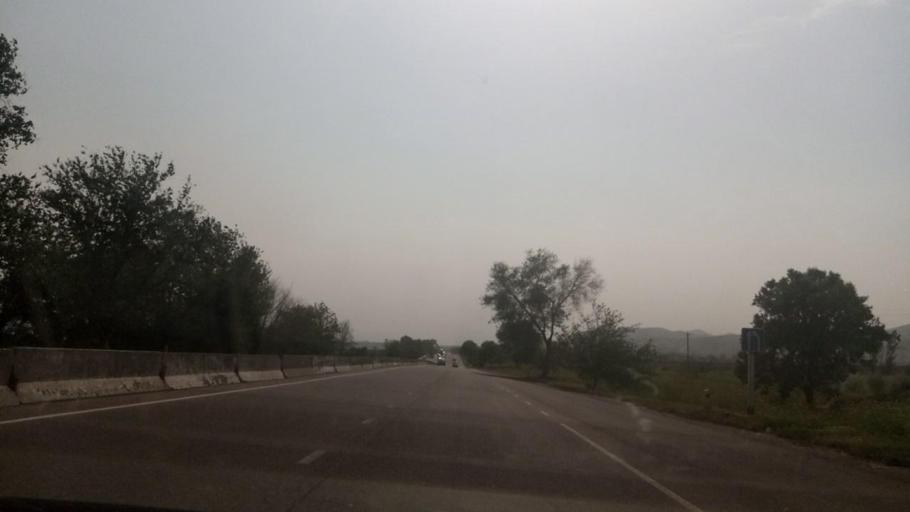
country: UZ
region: Toshkent
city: Angren
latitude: 40.9562
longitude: 69.9310
